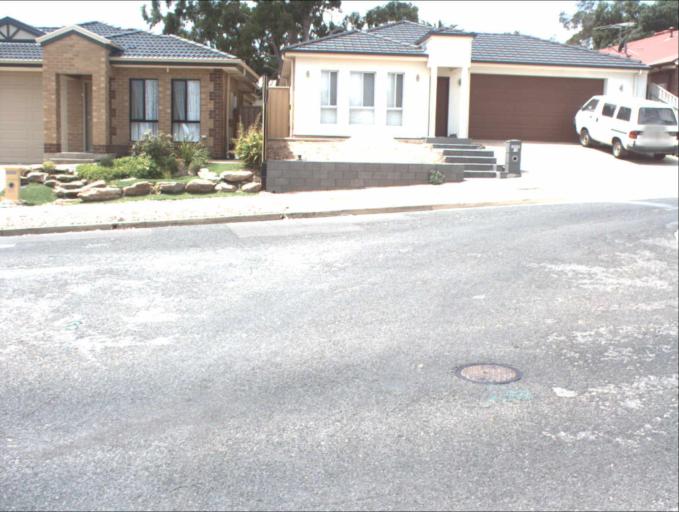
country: AU
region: South Australia
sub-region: Port Adelaide Enfield
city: Enfield
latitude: -34.8500
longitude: 138.6083
